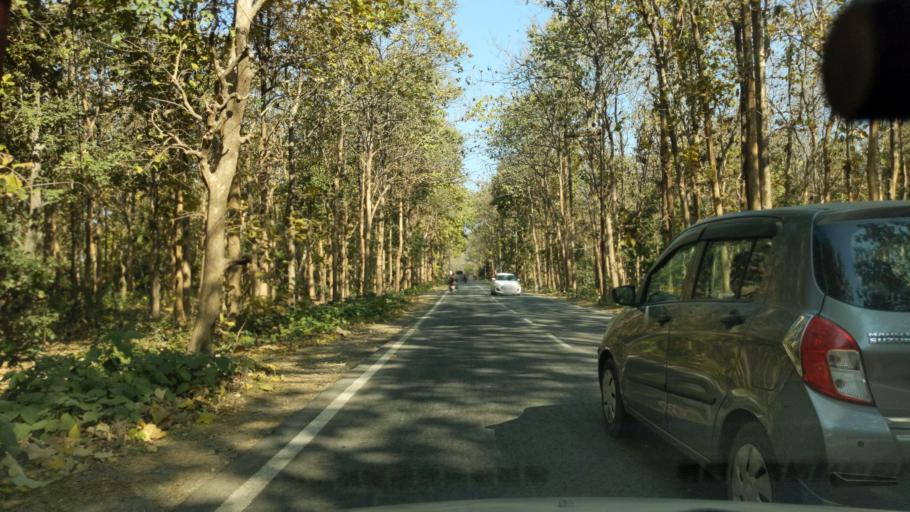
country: IN
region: Uttarakhand
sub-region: Naini Tal
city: Ramnagar
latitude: 29.3819
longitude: 79.1428
